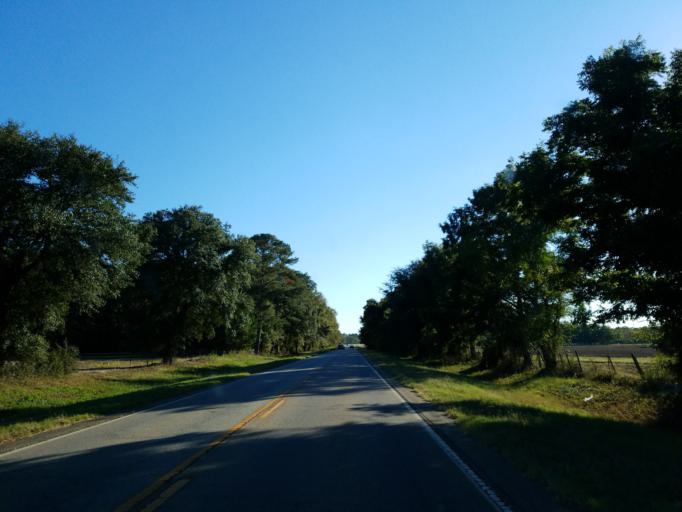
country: US
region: Georgia
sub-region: Lee County
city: Leesburg
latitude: 31.7562
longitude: -84.1532
